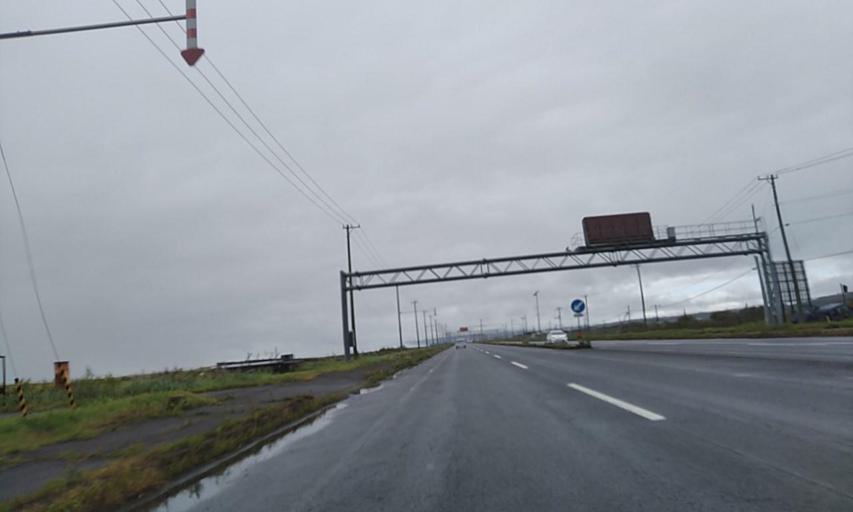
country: JP
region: Hokkaido
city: Kushiro
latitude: 43.0023
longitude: 144.2496
